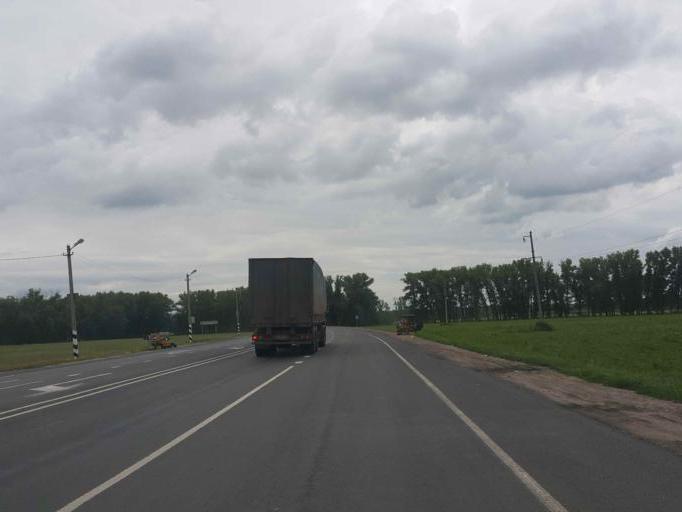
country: RU
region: Tambov
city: Zavoronezhskoye
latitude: 52.9538
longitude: 40.5799
